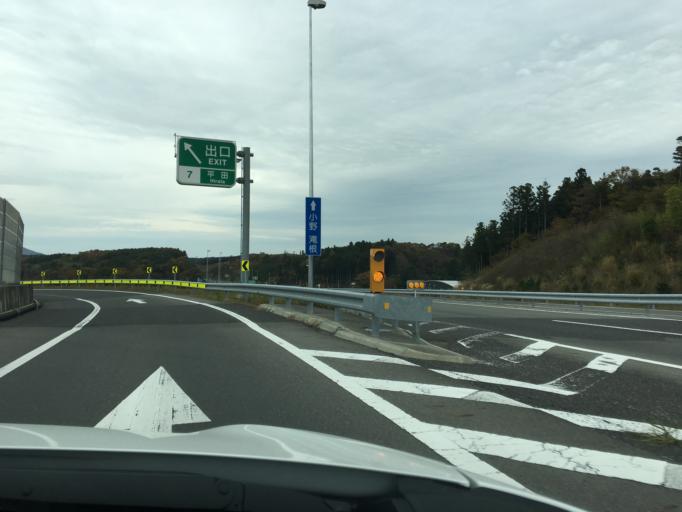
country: JP
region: Fukushima
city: Ishikawa
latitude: 37.2457
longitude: 140.5586
